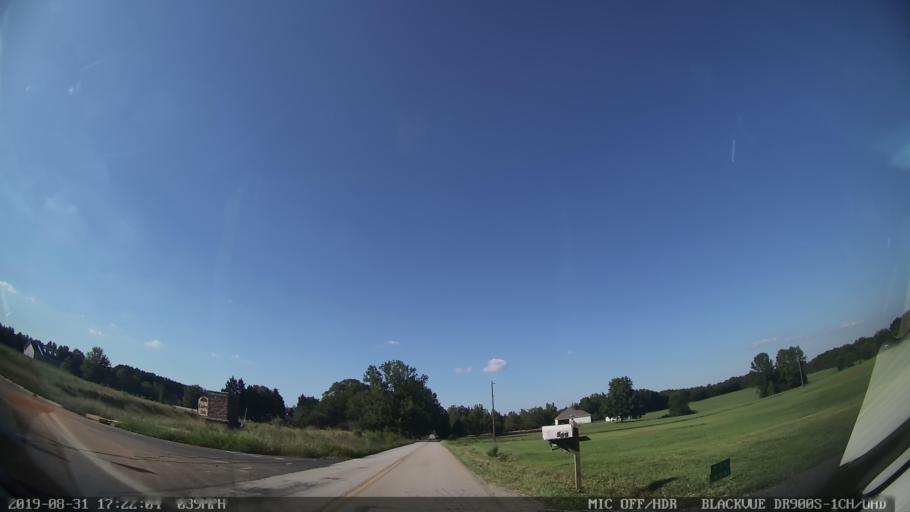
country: US
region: South Carolina
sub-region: Spartanburg County
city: Boiling Springs
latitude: 35.0714
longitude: -81.9383
